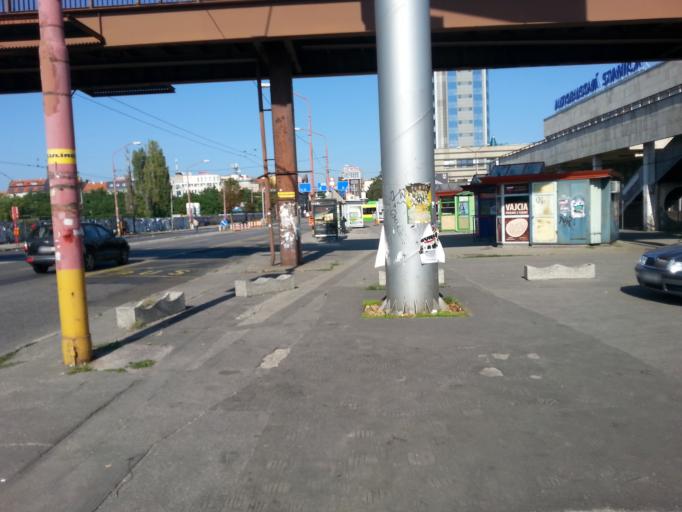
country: SK
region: Bratislavsky
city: Bratislava
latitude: 48.1463
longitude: 17.1274
